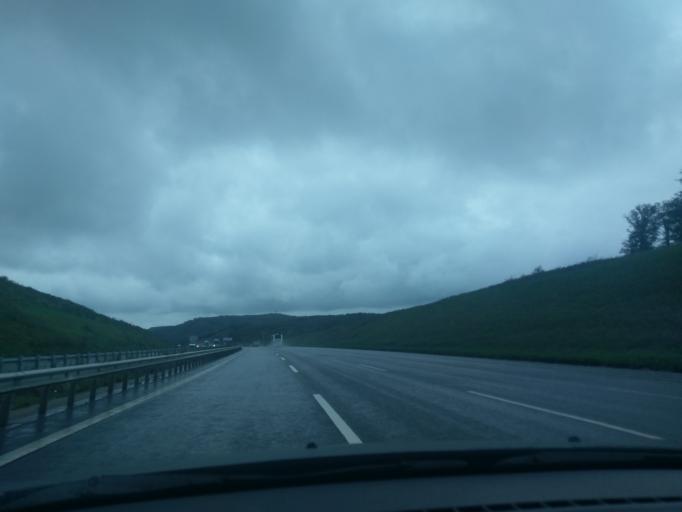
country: TR
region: Istanbul
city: Arikoey
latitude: 41.2306
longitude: 28.9334
